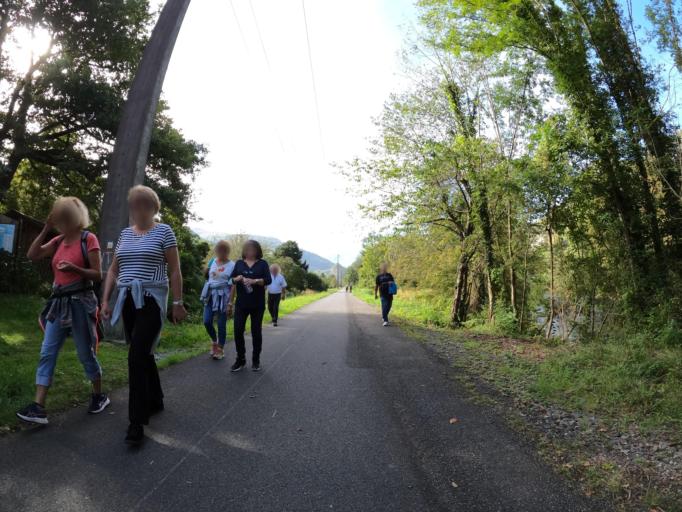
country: FR
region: Midi-Pyrenees
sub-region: Departement des Hautes-Pyrenees
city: Lourdes
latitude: 43.0585
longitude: -0.0419
